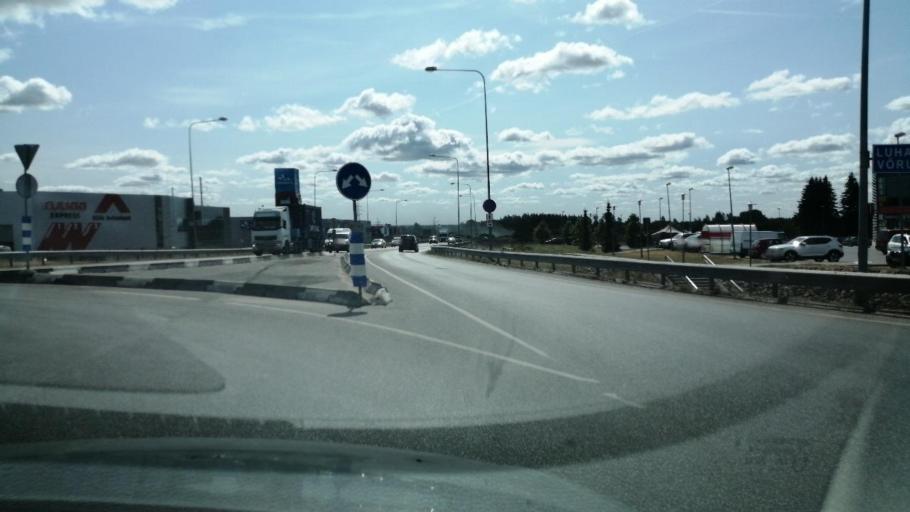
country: EE
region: Tartu
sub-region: Tartu linn
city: Tartu
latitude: 58.3526
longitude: 26.6901
